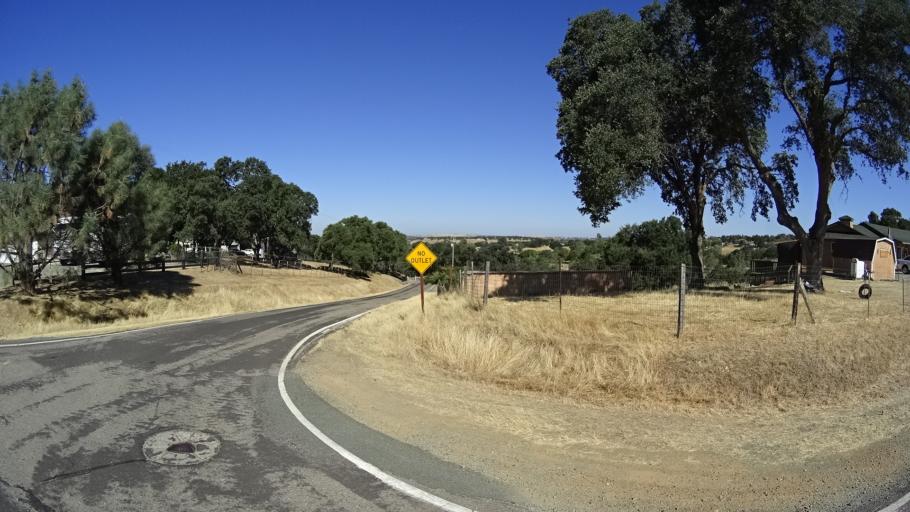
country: US
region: California
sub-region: Calaveras County
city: Rancho Calaveras
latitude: 38.0950
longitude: -120.8625
